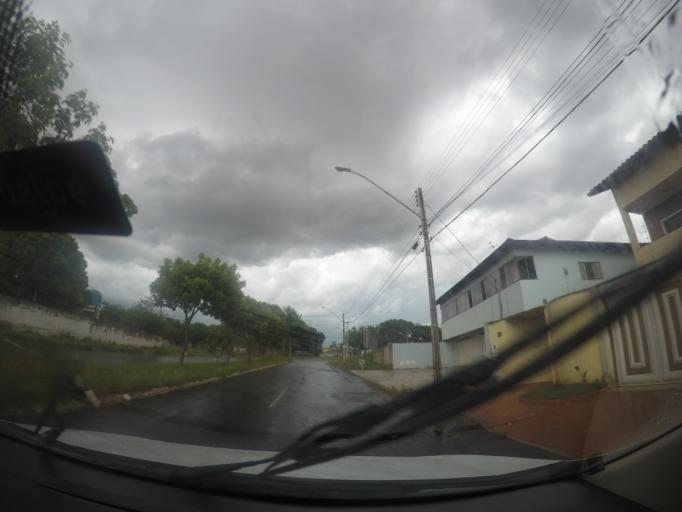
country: BR
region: Goias
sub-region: Goiania
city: Goiania
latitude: -16.6426
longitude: -49.2357
